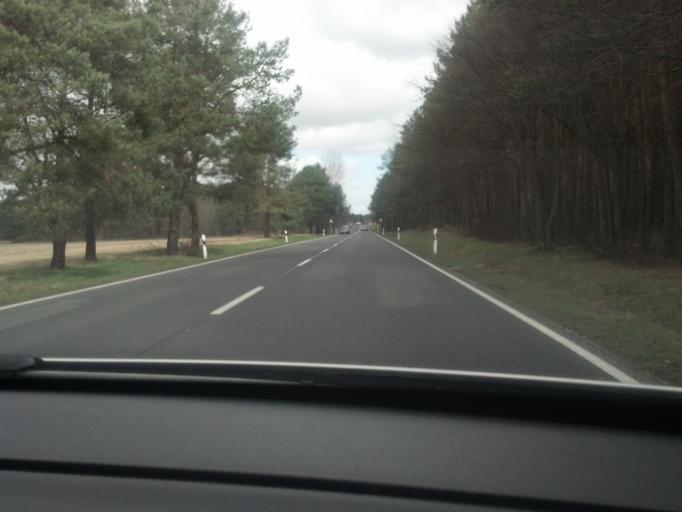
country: DE
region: Mecklenburg-Vorpommern
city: Wesenberg
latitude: 53.2963
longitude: 13.0372
